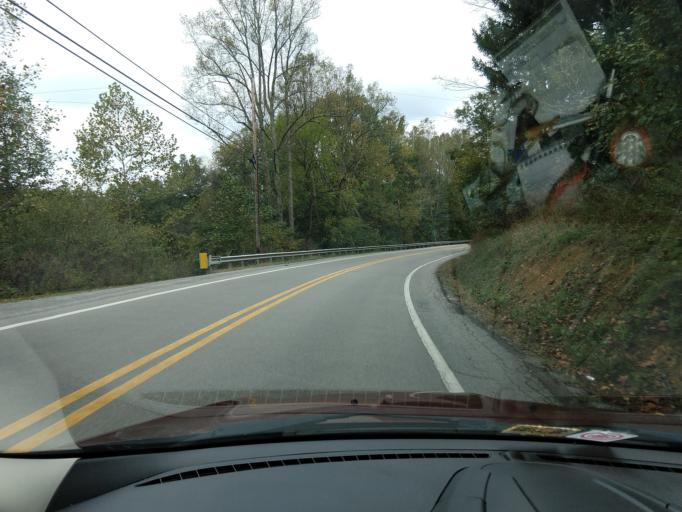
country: US
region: West Virginia
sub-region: Barbour County
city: Belington
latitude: 39.0047
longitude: -79.9402
